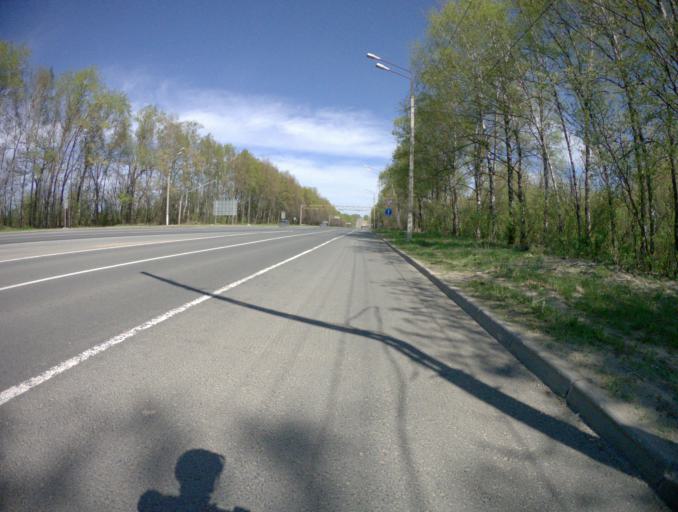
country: RU
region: Vladimir
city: Bogolyubovo
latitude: 56.1764
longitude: 40.4999
